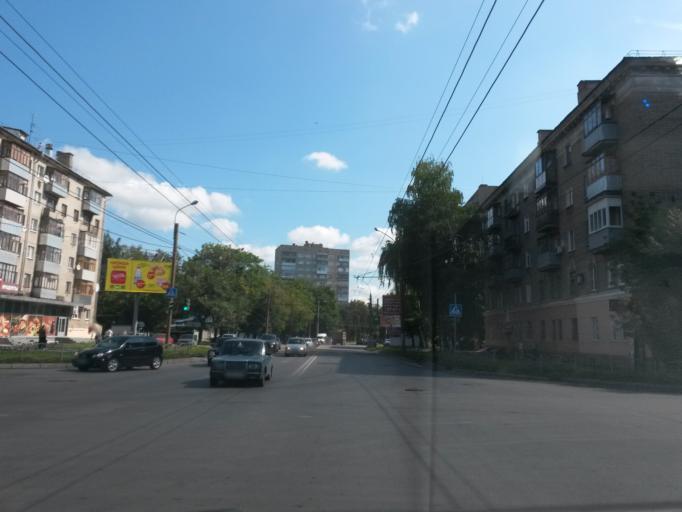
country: RU
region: Ivanovo
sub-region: Gorod Ivanovo
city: Ivanovo
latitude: 57.0110
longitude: 40.9791
